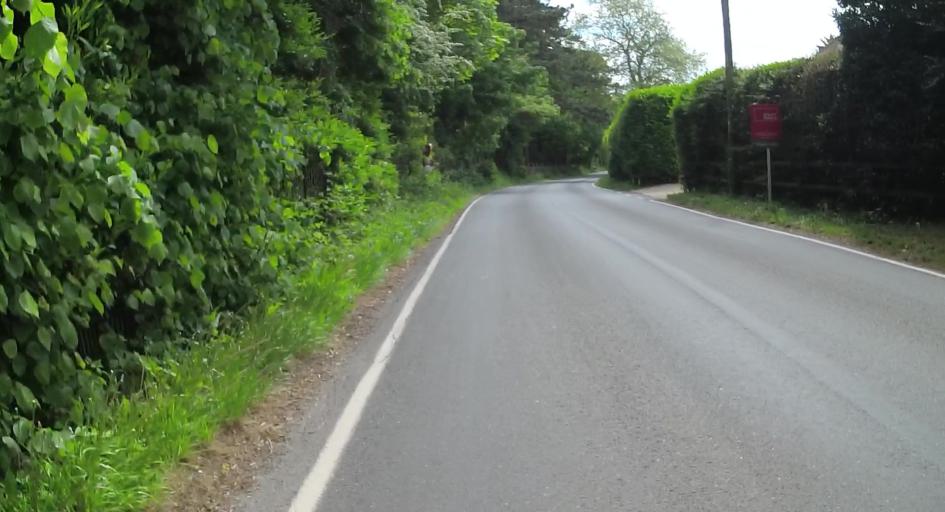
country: GB
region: England
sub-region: Surrey
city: Farnham
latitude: 51.2340
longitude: -0.8328
